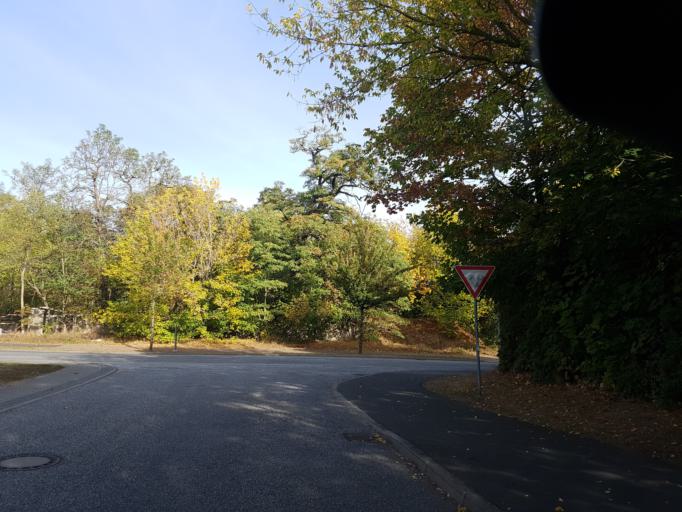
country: DE
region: Brandenburg
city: Juterbog
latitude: 52.0010
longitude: 13.0487
